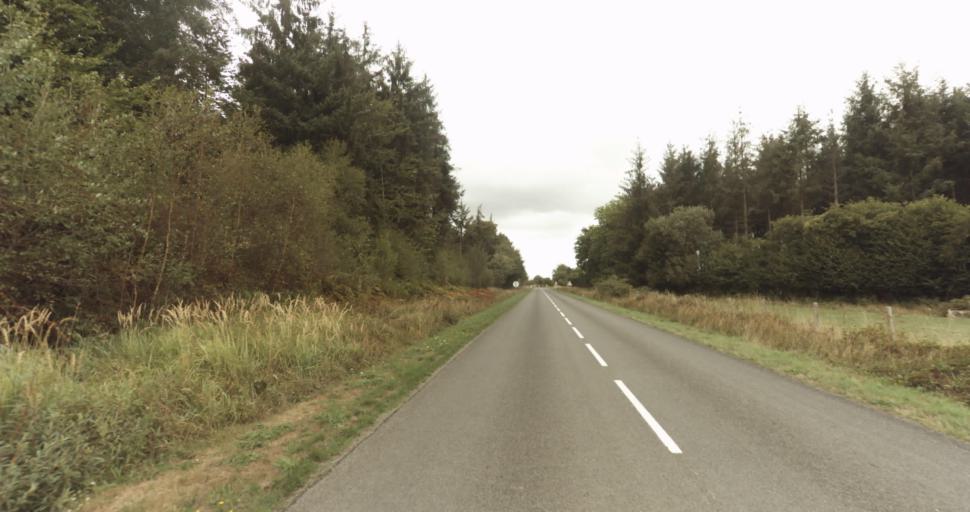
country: FR
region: Lower Normandy
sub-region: Departement de l'Orne
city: Gace
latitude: 48.8007
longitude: 0.3438
